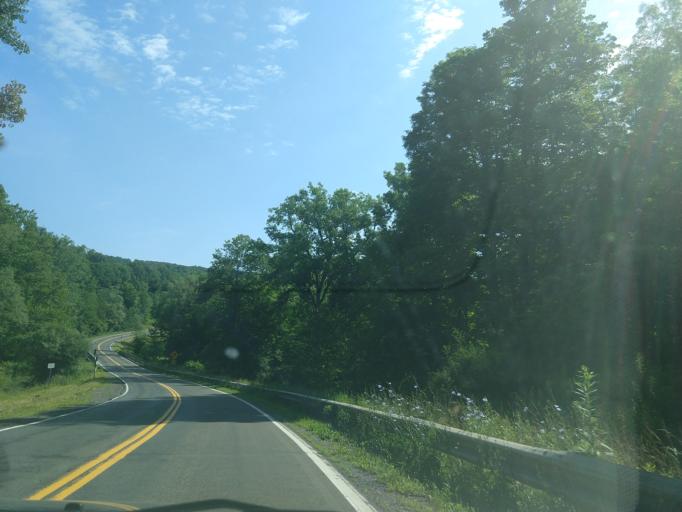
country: US
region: New York
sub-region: Tompkins County
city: East Ithaca
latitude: 42.4104
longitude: -76.4548
